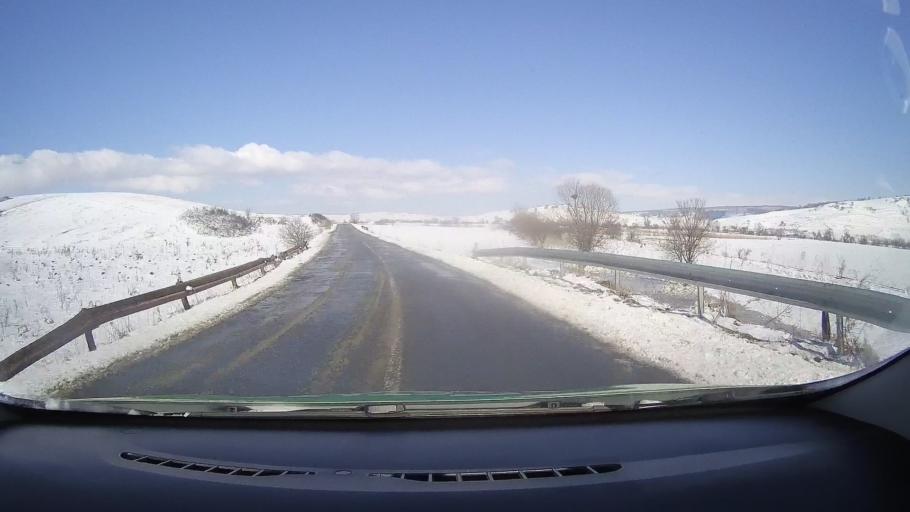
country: RO
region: Sibiu
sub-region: Comuna Rosia
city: Rosia
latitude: 45.8252
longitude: 24.3143
